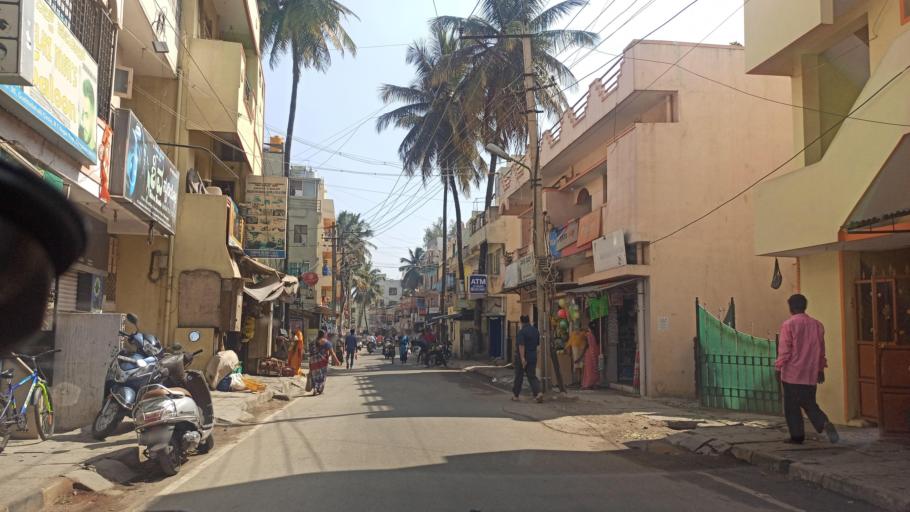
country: IN
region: Karnataka
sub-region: Bangalore Urban
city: Yelahanka
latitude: 13.0390
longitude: 77.5980
